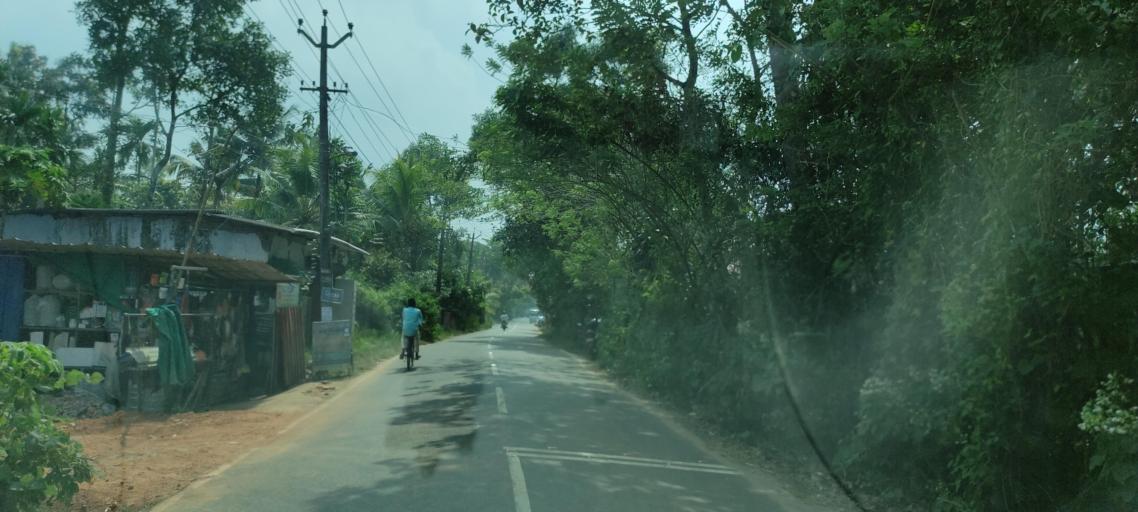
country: IN
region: Kerala
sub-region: Alappuzha
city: Alleppey
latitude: 9.5517
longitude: 76.3333
